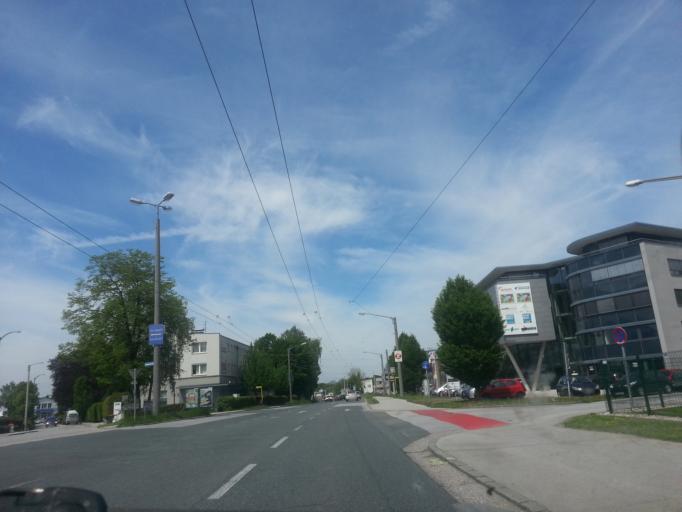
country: DE
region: Bavaria
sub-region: Upper Bavaria
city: Freilassing
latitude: 47.8300
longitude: 13.0028
